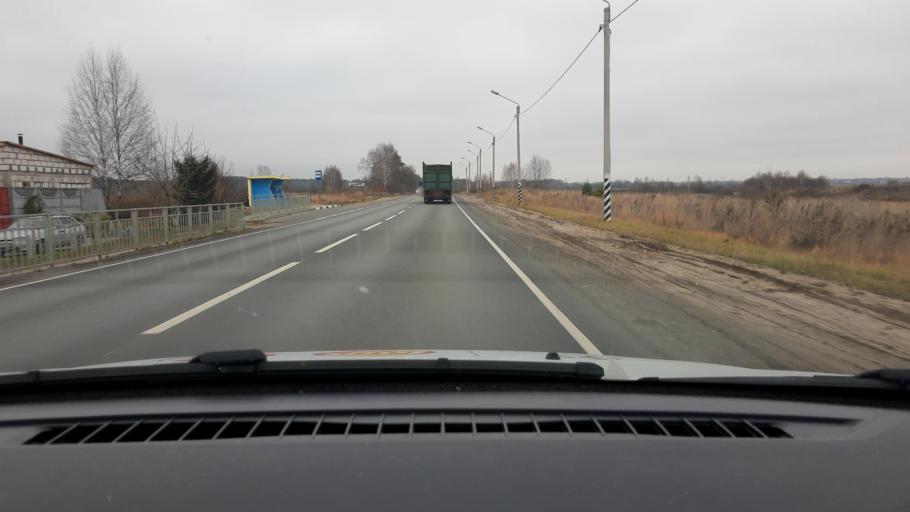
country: RU
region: Nizjnij Novgorod
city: Gidrotorf
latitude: 56.5540
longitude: 43.5139
